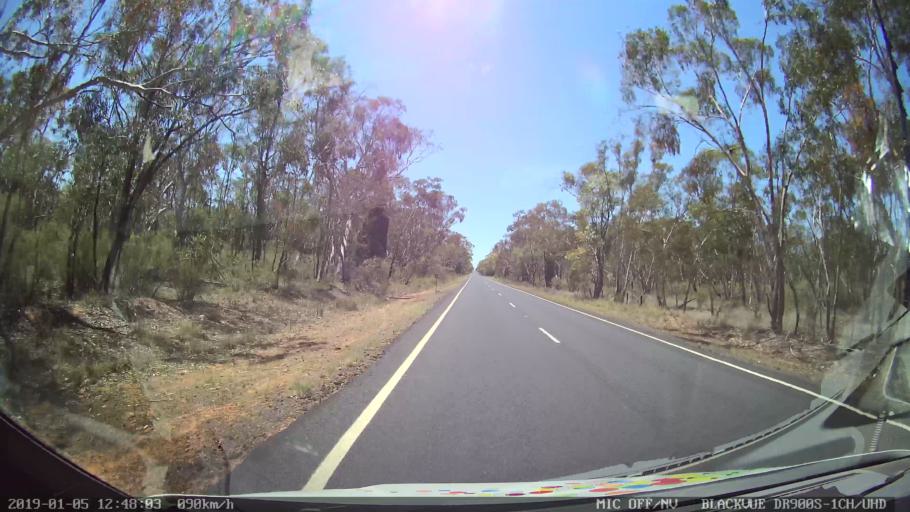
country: AU
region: New South Wales
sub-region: Warrumbungle Shire
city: Coonabarabran
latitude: -31.1181
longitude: 149.5860
